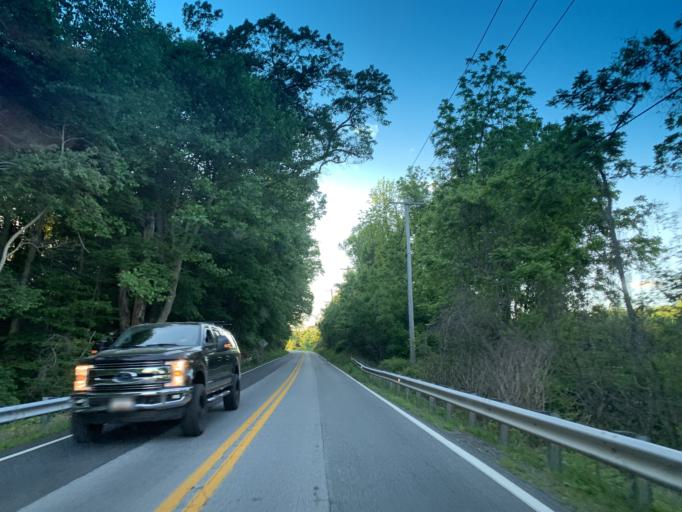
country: US
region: Maryland
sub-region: Cecil County
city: Elkton
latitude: 39.7109
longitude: -75.8691
